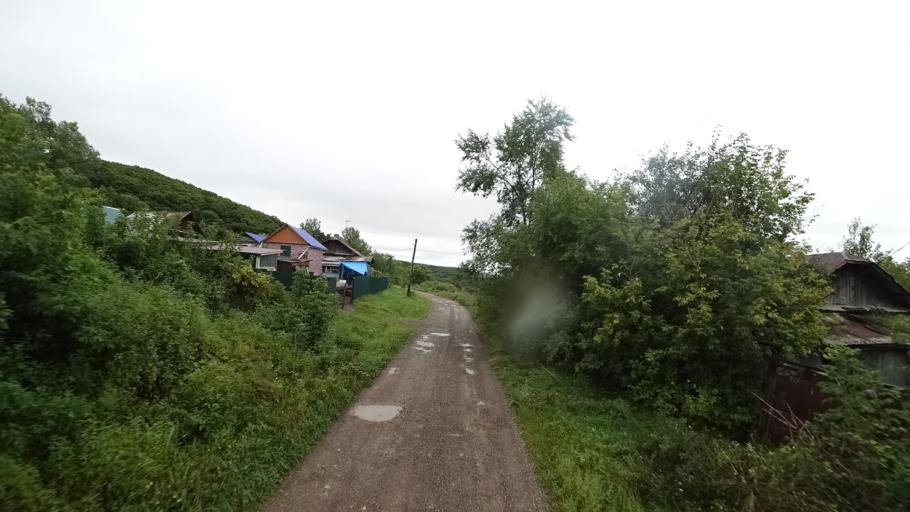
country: RU
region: Primorskiy
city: Monastyrishche
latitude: 44.2623
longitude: 132.4052
